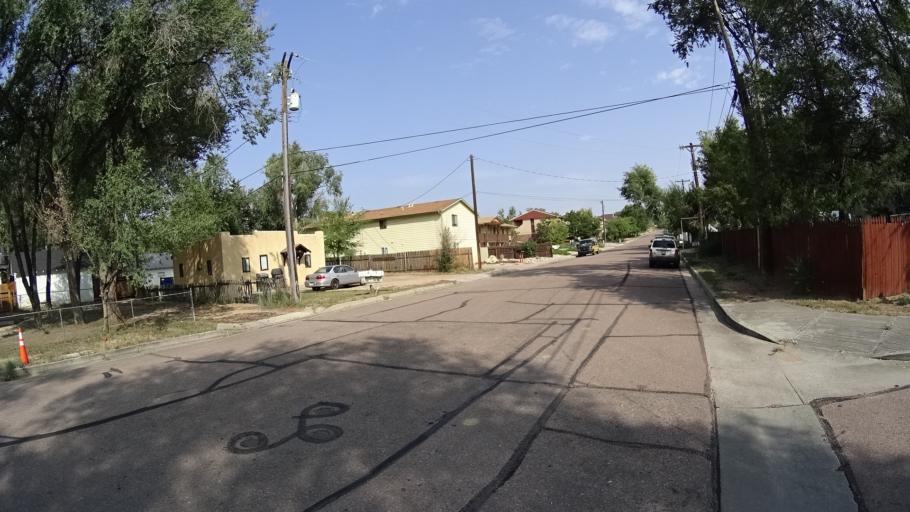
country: US
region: Colorado
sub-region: El Paso County
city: Colorado Springs
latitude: 38.8422
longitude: -104.7825
